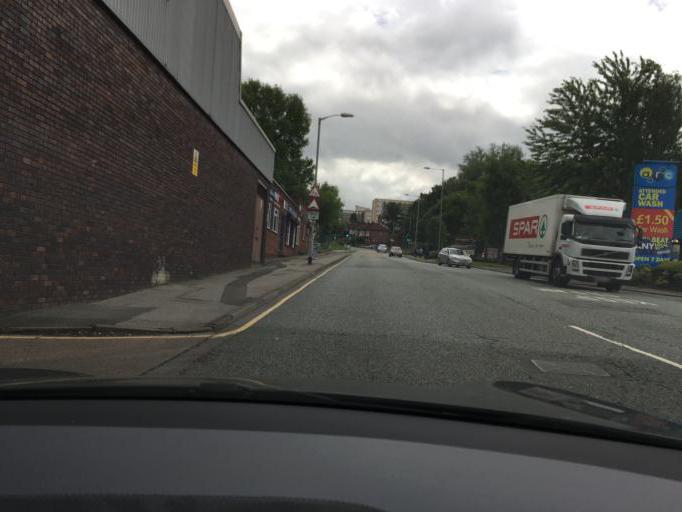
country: GB
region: England
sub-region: Borough of Stockport
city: Stockport
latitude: 53.4067
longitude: -2.1662
